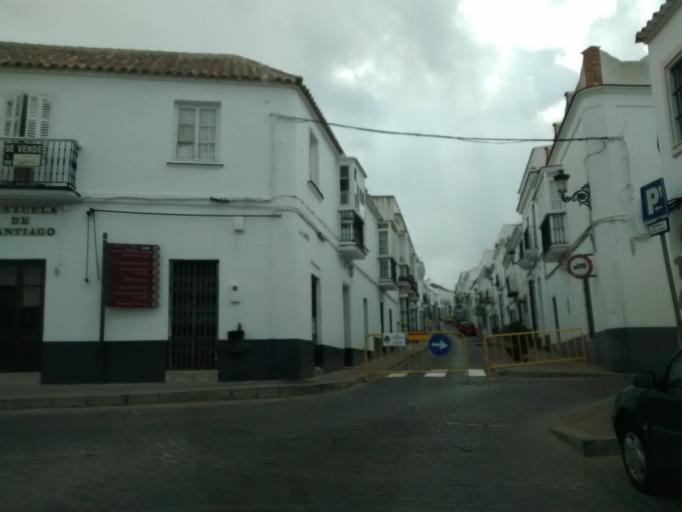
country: ES
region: Andalusia
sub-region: Provincia de Cadiz
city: Medina Sidonia
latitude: 36.4588
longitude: -5.9300
